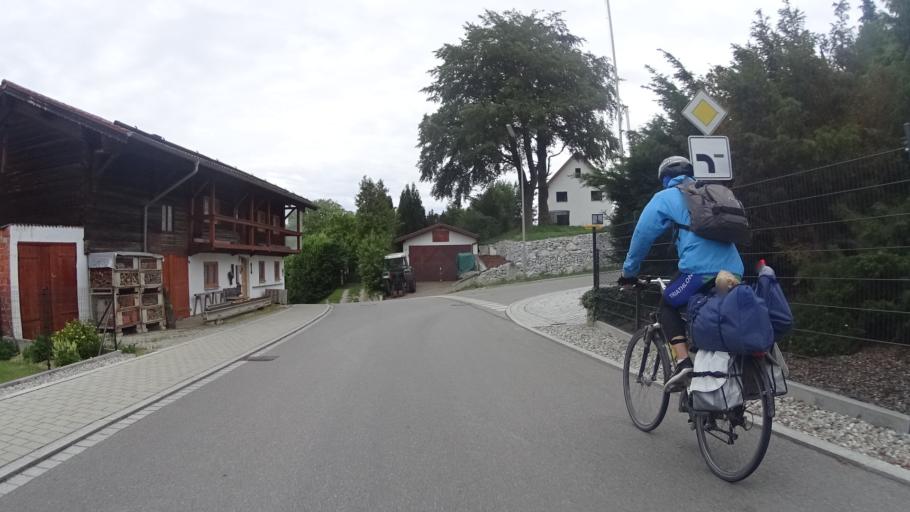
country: DE
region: Bavaria
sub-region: Lower Bavaria
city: Wurmsham
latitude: 48.3838
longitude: 12.3103
